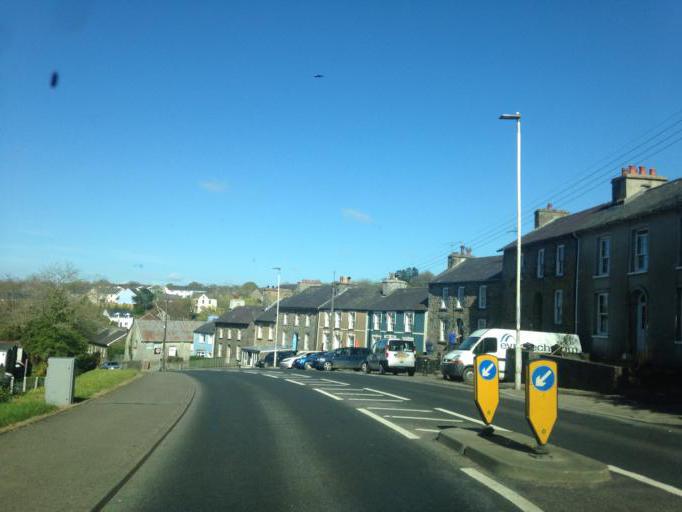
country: GB
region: Wales
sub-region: County of Ceredigion
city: Llanarth
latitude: 52.1929
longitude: -4.3091
